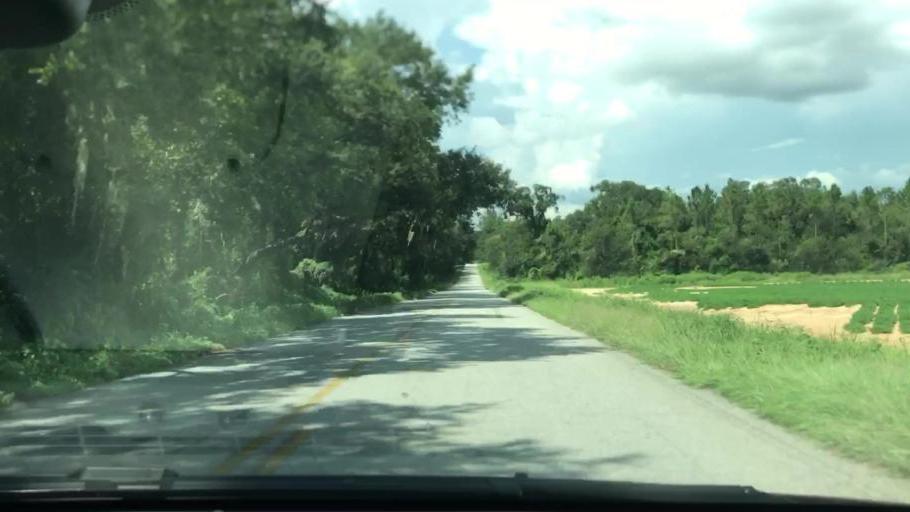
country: US
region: Georgia
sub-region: Seminole County
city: Donalsonville
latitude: 30.9857
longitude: -84.9768
